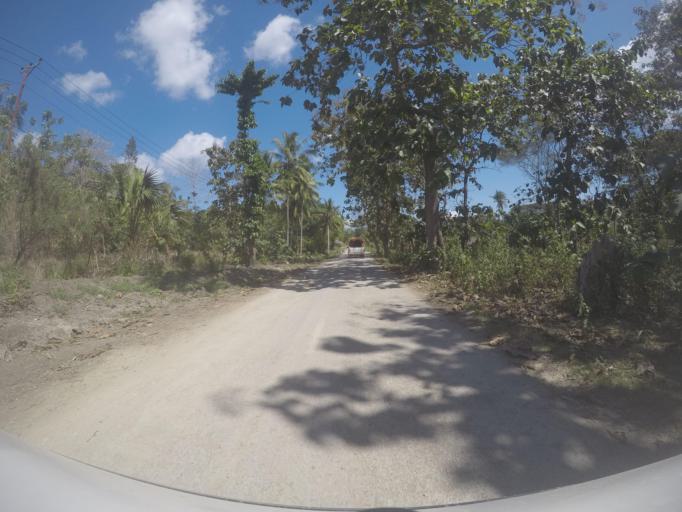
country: TL
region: Viqueque
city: Viqueque
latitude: -8.9162
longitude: 126.3974
